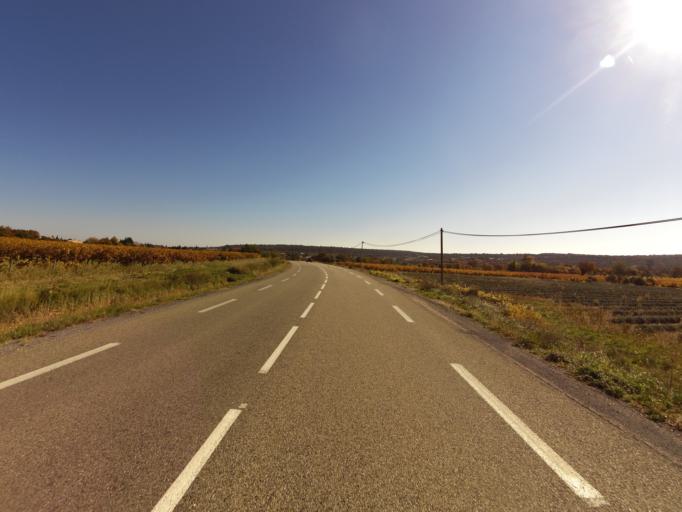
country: FR
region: Languedoc-Roussillon
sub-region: Departement du Gard
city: Saint-Julien-de-Peyrolas
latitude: 44.3964
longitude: 4.4842
